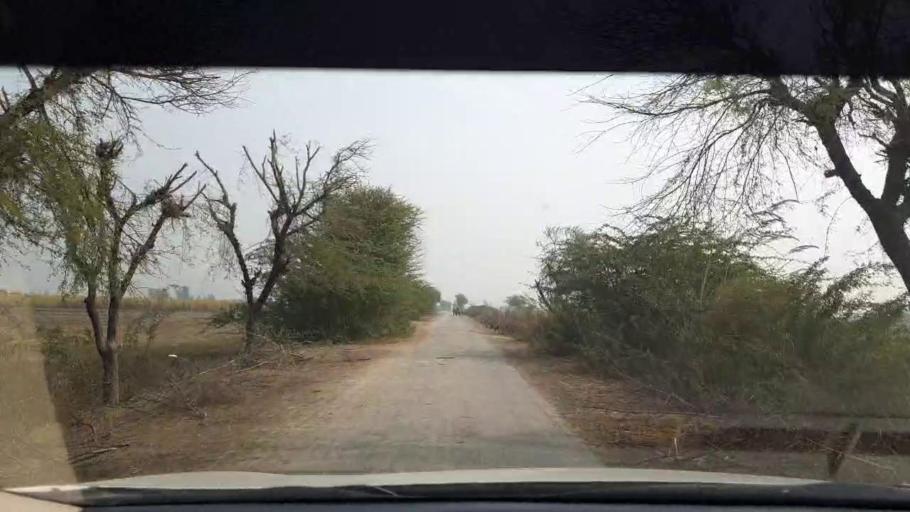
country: PK
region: Sindh
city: Berani
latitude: 25.8472
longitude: 68.8220
